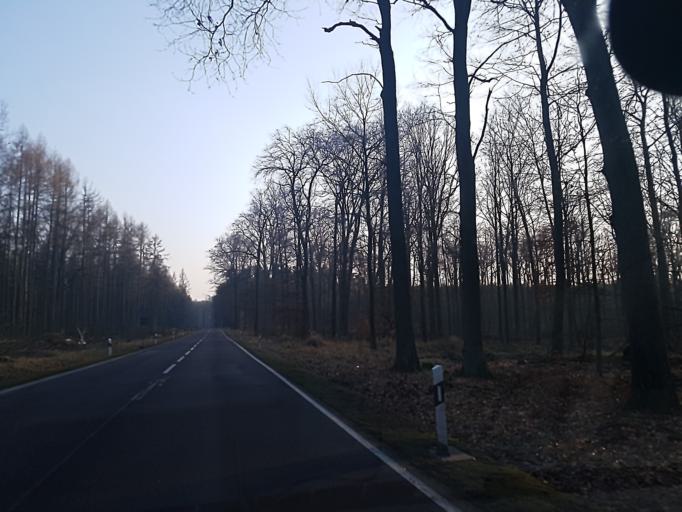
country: DE
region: Brandenburg
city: Wiesenburg
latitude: 52.0335
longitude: 12.4556
